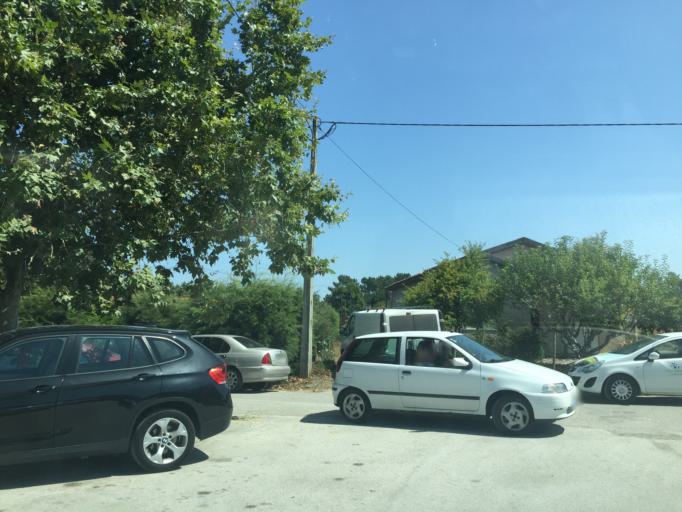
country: PT
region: Coimbra
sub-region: Mira
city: Mira
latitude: 40.3414
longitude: -8.7272
